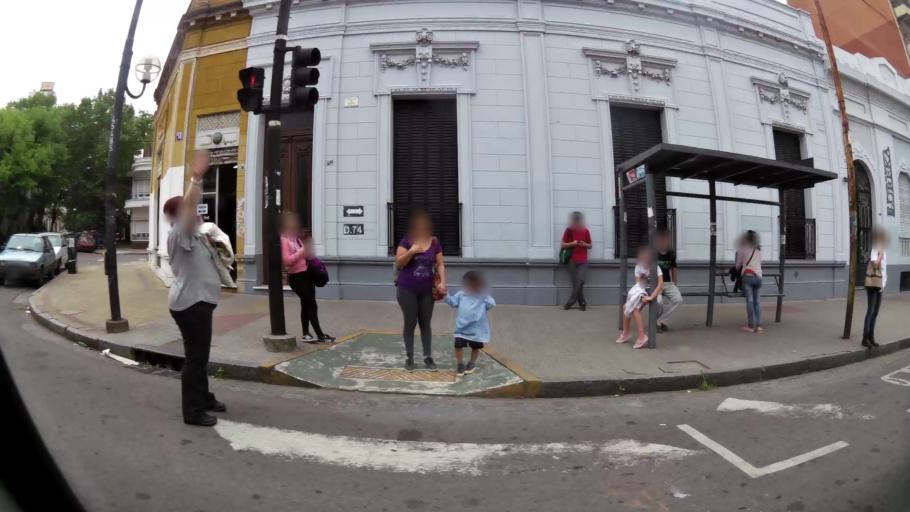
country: AR
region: Buenos Aires
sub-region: Partido de La Plata
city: La Plata
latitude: -34.9273
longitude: -57.9542
